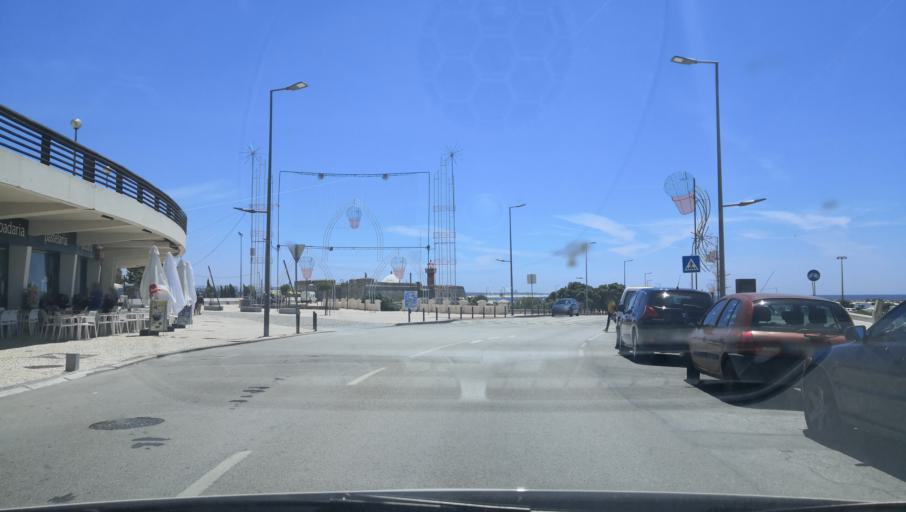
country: PT
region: Coimbra
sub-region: Figueira da Foz
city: Figueira da Foz
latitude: 40.1497
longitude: -8.8665
